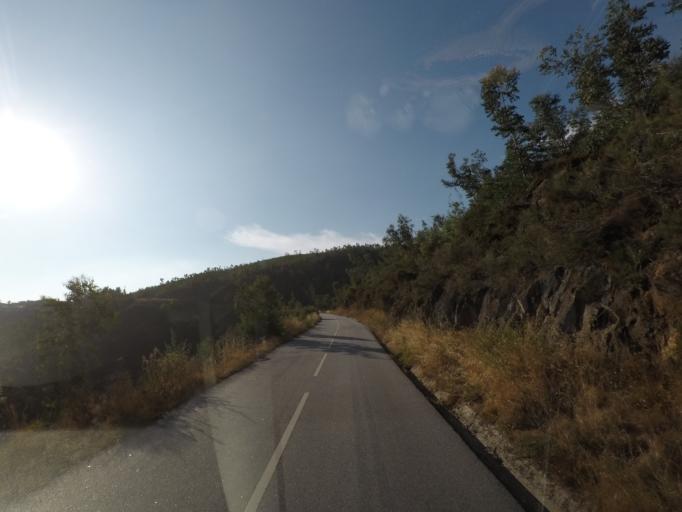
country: PT
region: Vila Real
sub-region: Mesao Frio
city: Mesao Frio
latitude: 41.1639
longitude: -7.9081
